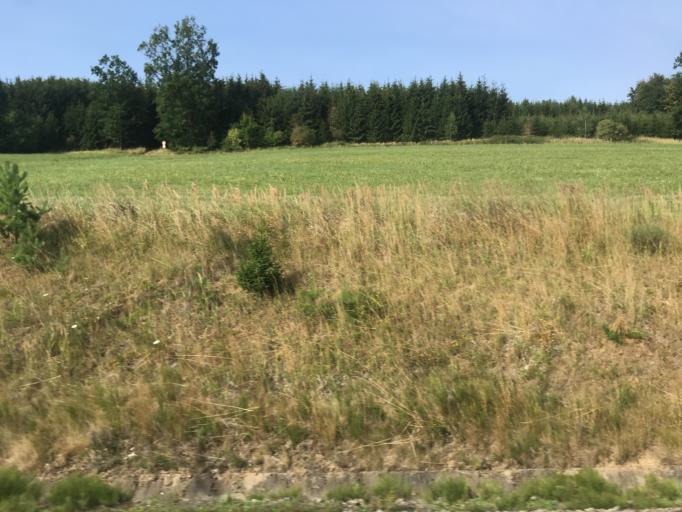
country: CZ
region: Central Bohemia
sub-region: Okres Benesov
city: Benesov
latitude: 49.8097
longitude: 14.7087
